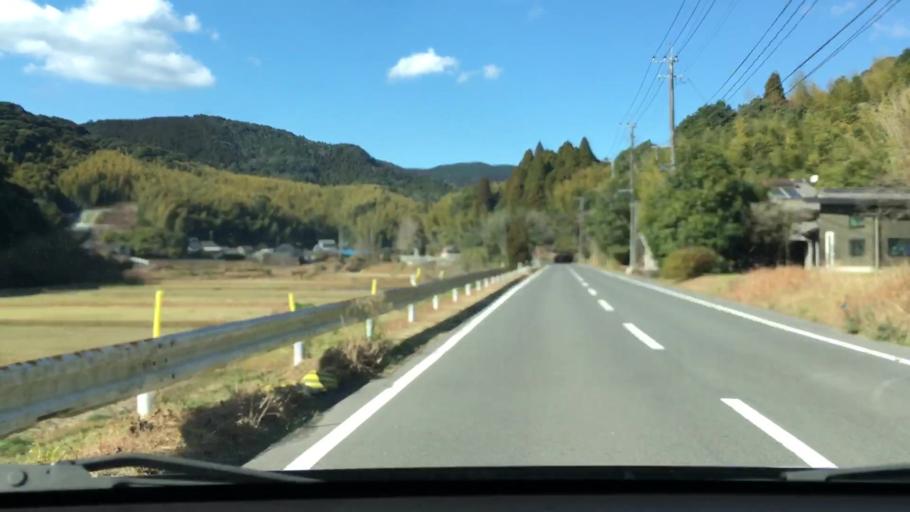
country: JP
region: Kagoshima
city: Ijuin
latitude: 31.7054
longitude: 130.4458
